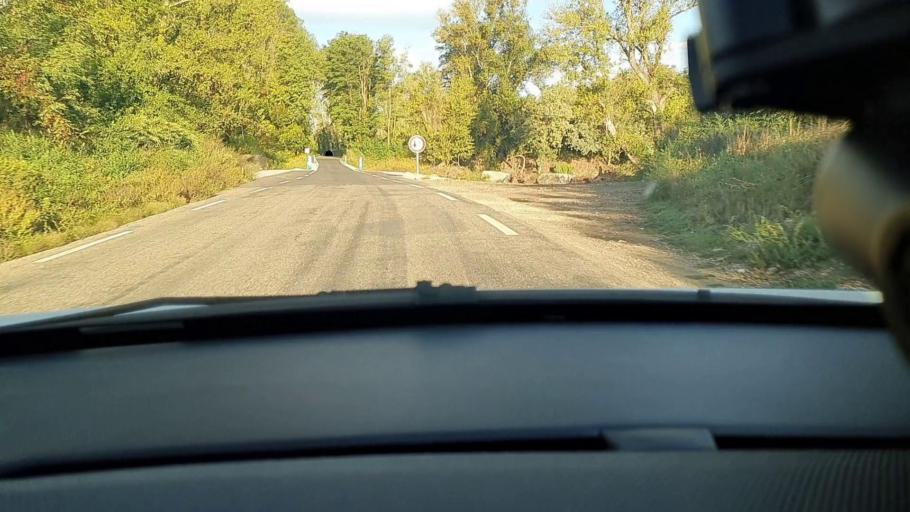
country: FR
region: Languedoc-Roussillon
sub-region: Departement du Gard
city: Saint-Ambroix
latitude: 44.2348
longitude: 4.2744
